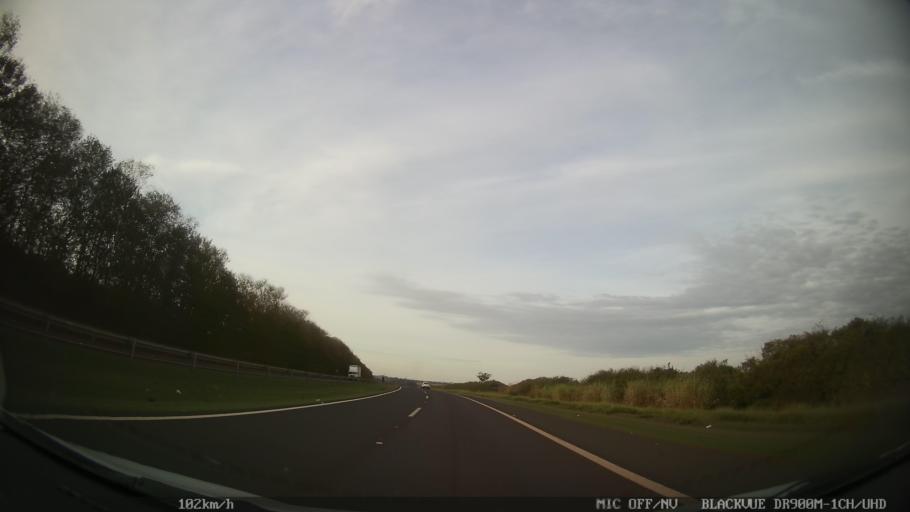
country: BR
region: Sao Paulo
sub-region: Iracemapolis
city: Iracemapolis
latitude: -22.6679
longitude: -47.5381
